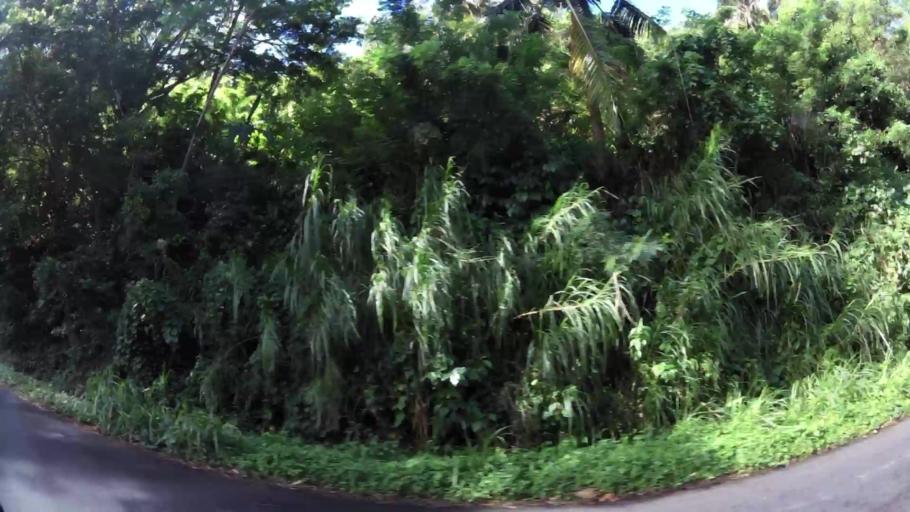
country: LC
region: Soufriere
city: Soufriere
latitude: 13.8305
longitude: -61.0506
